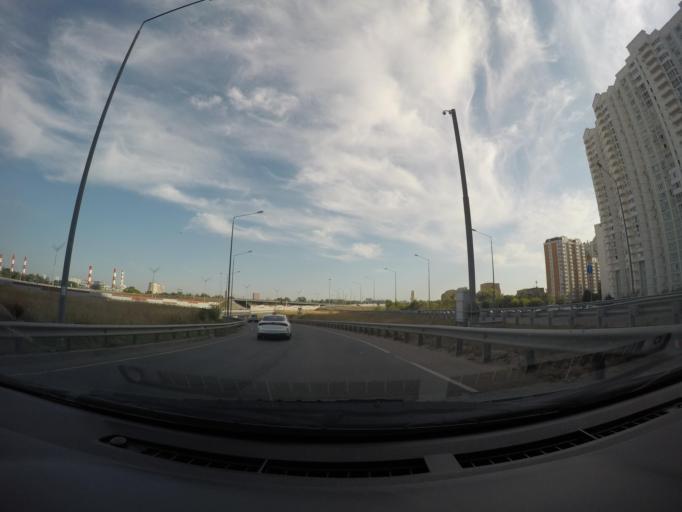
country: RU
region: Moskovskaya
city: Levoberezhnaya
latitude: 55.8995
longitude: 37.4845
